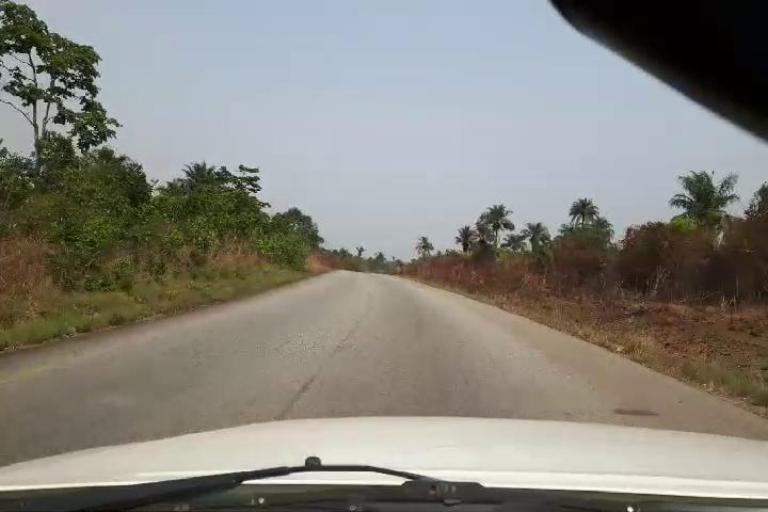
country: SL
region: Southern Province
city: Largo
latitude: 8.3017
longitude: -12.1998
